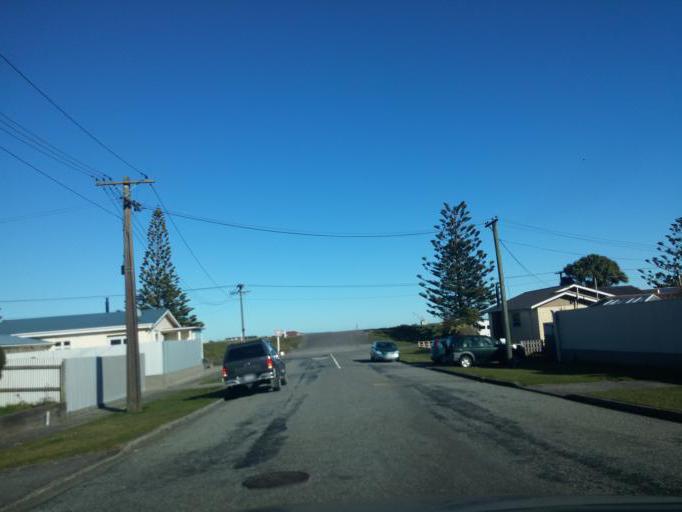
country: NZ
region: West Coast
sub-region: Grey District
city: Greymouth
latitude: -42.4424
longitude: 171.2111
